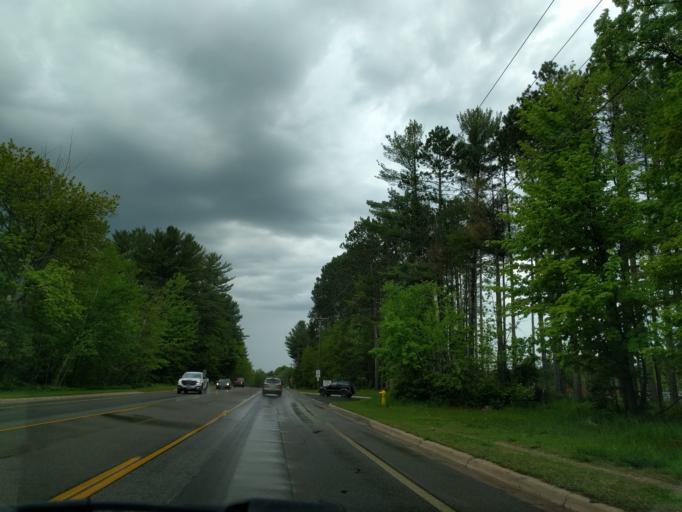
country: US
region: Michigan
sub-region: Marquette County
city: Trowbridge Park
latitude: 46.5643
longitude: -87.4327
